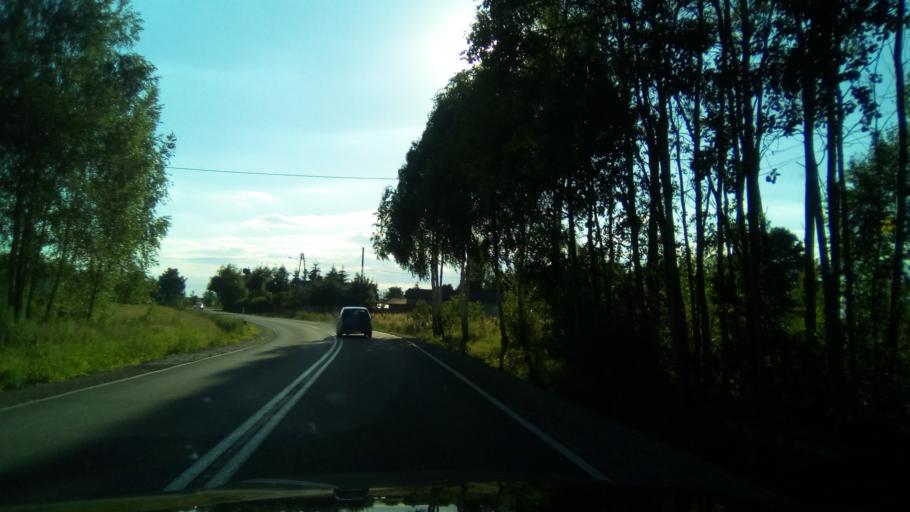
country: PL
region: Masovian Voivodeship
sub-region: Powiat radomski
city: Jastrzebia
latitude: 51.6176
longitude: 21.2160
